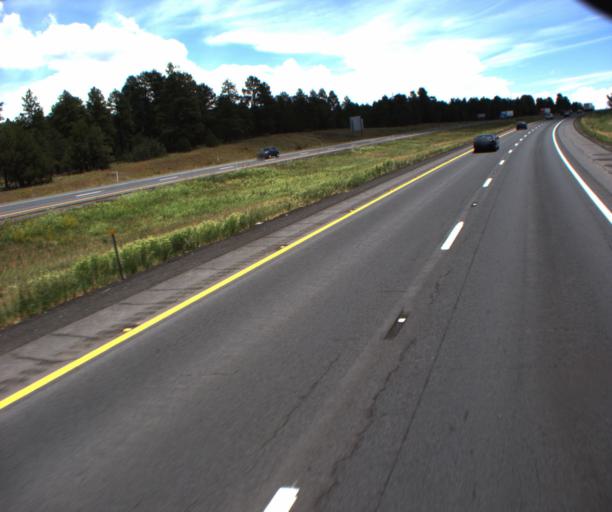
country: US
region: Arizona
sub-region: Coconino County
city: Williams
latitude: 35.2638
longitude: -112.1623
